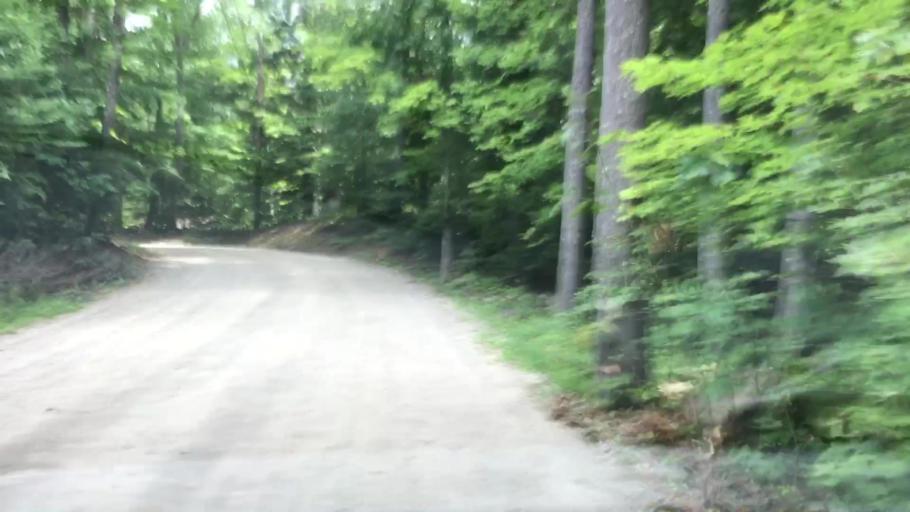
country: US
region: New Hampshire
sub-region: Hillsborough County
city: Mont Vernon
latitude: 42.8868
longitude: -71.6172
